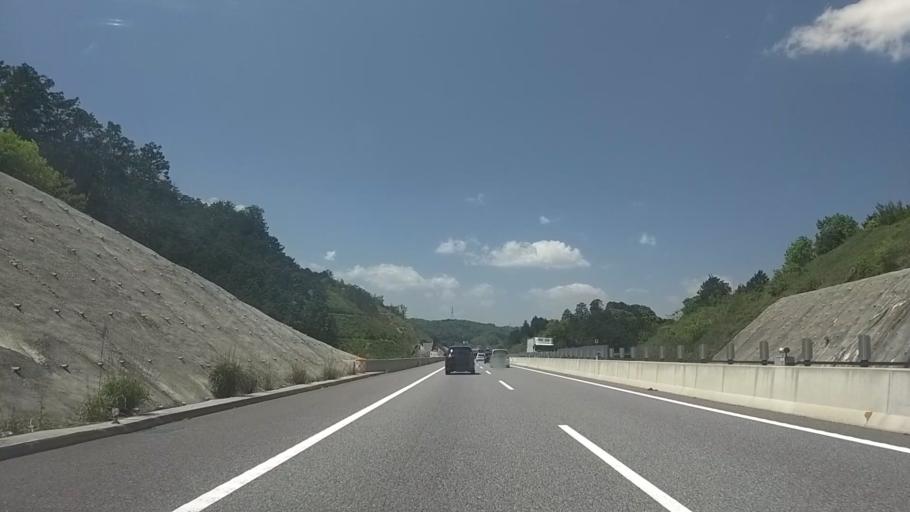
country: JP
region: Aichi
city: Gamagori
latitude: 34.9091
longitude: 137.2956
